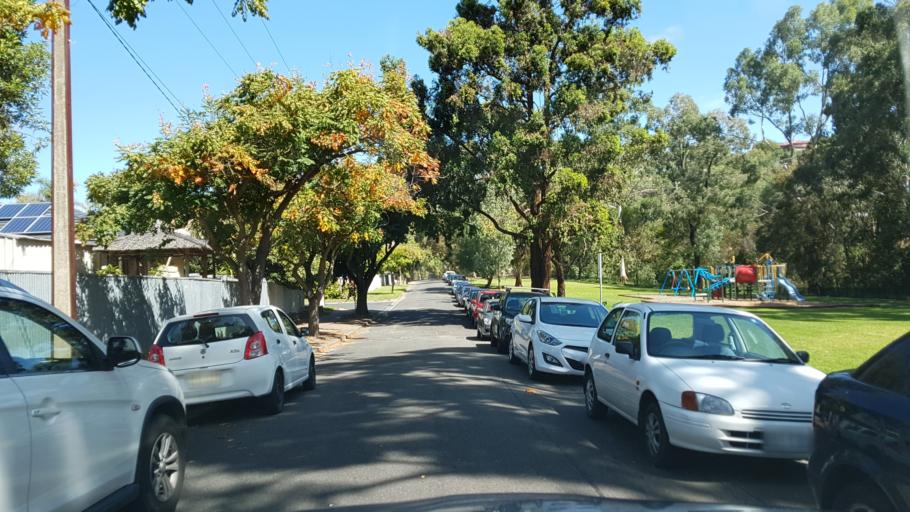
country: AU
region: South Australia
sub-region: Onkaparinga
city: Bedford Park
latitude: -35.0265
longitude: 138.5639
